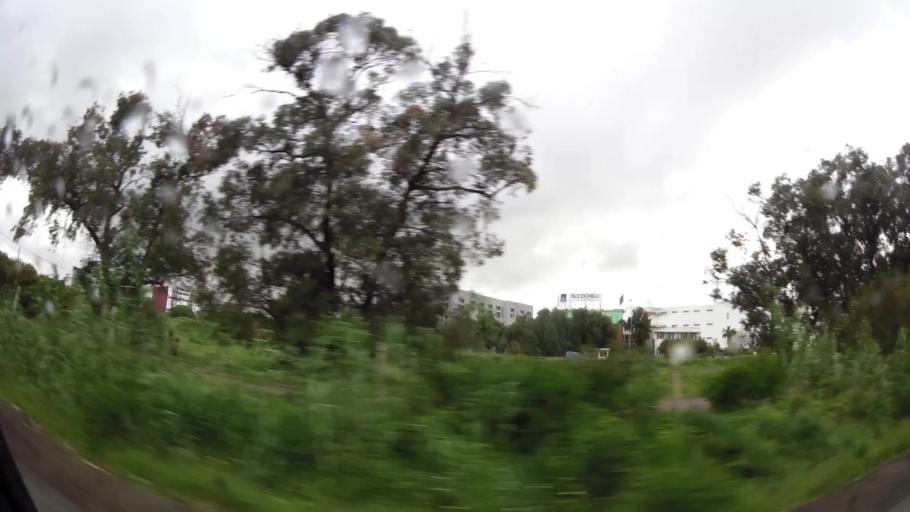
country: MA
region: Grand Casablanca
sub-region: Mohammedia
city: Mohammedia
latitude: 33.6628
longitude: -7.4046
